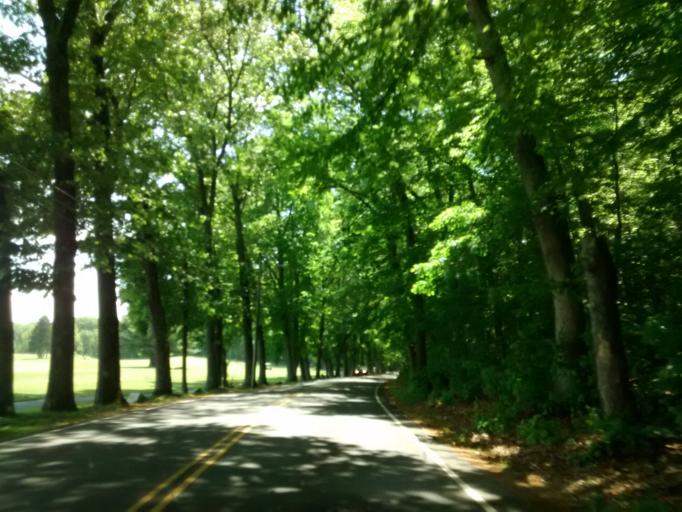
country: US
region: Massachusetts
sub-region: Worcester County
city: Whitinsville
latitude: 42.1048
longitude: -71.6594
